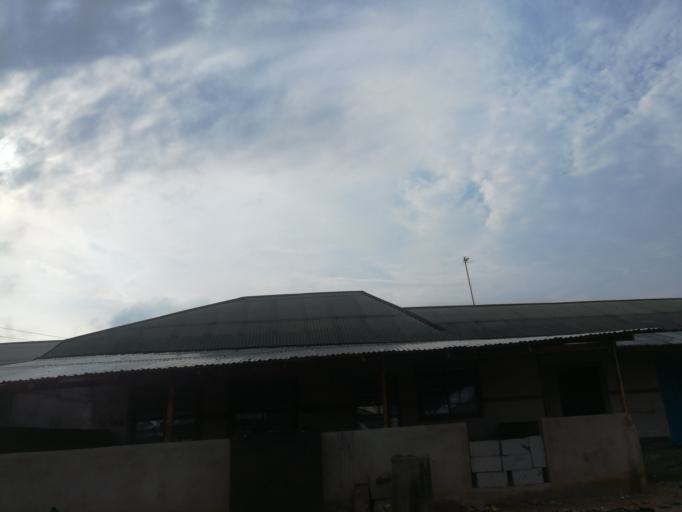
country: NG
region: Rivers
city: Okrika
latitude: 4.7638
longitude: 7.0963
